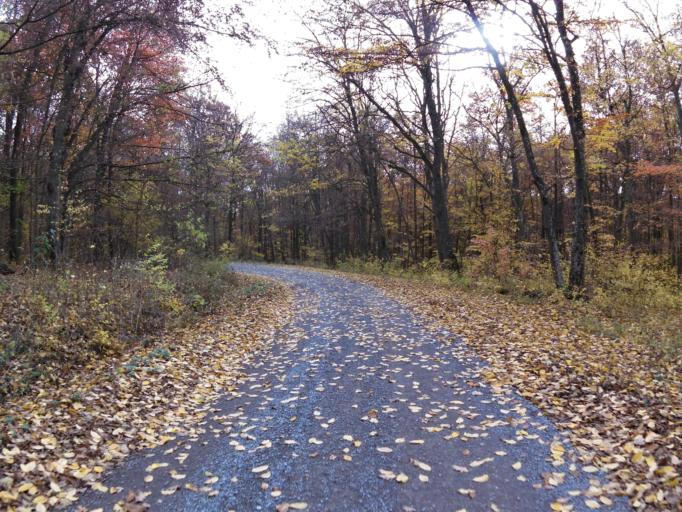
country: DE
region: Bavaria
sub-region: Regierungsbezirk Unterfranken
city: Waldbrunn
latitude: 49.7497
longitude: 9.8062
